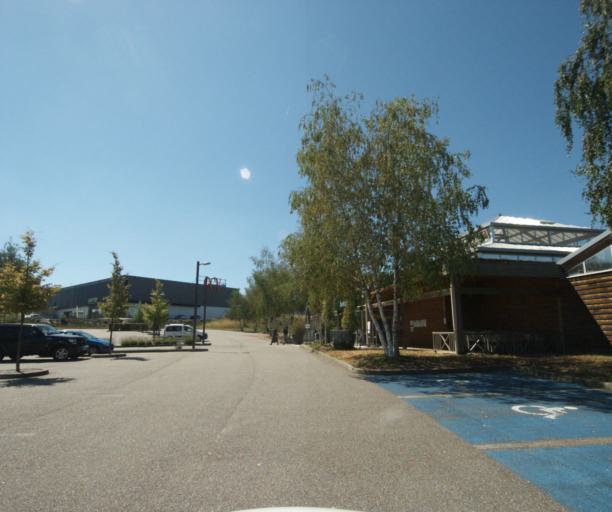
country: FR
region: Lorraine
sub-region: Departement des Vosges
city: Epinal
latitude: 48.1894
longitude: 6.4702
